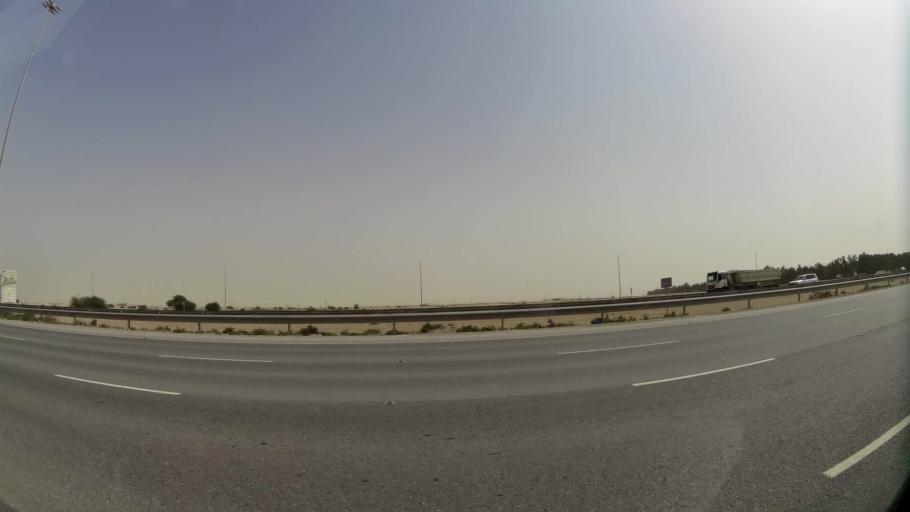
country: QA
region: Baladiyat ar Rayyan
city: Ar Rayyan
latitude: 25.1659
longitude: 51.3082
